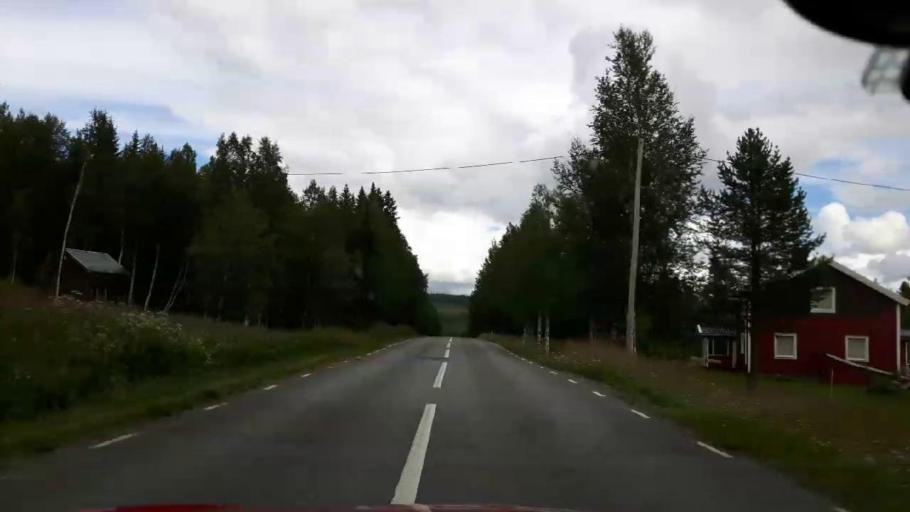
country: NO
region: Nord-Trondelag
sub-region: Lierne
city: Sandvika
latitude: 64.3921
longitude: 14.4779
